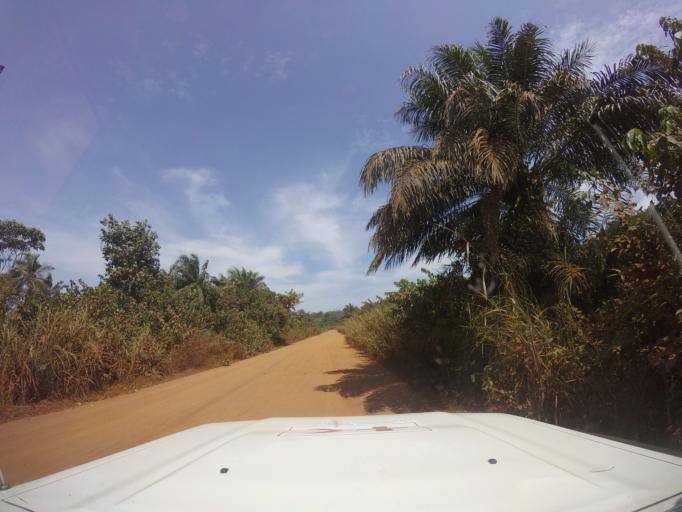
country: LR
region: Grand Cape Mount
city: Robertsport
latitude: 6.7478
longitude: -11.3542
